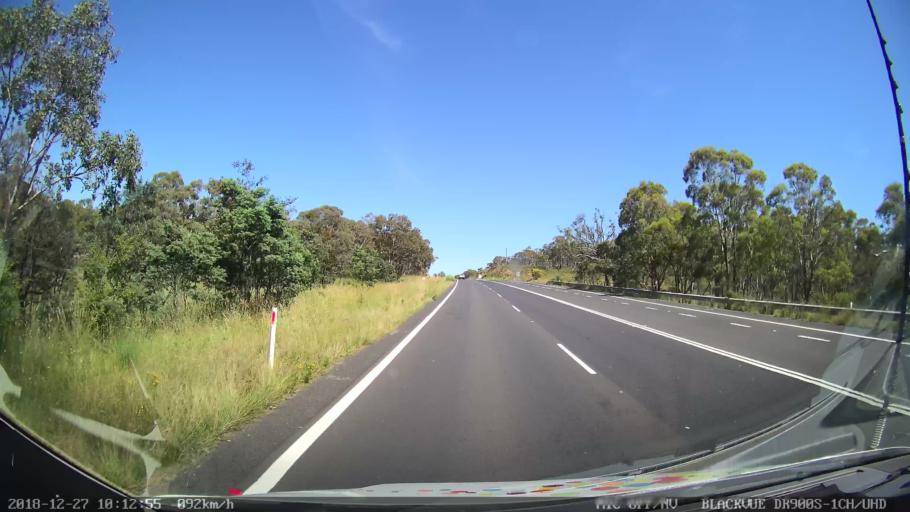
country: AU
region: New South Wales
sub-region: Bathurst Regional
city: Kelso
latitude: -33.4382
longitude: 149.7547
